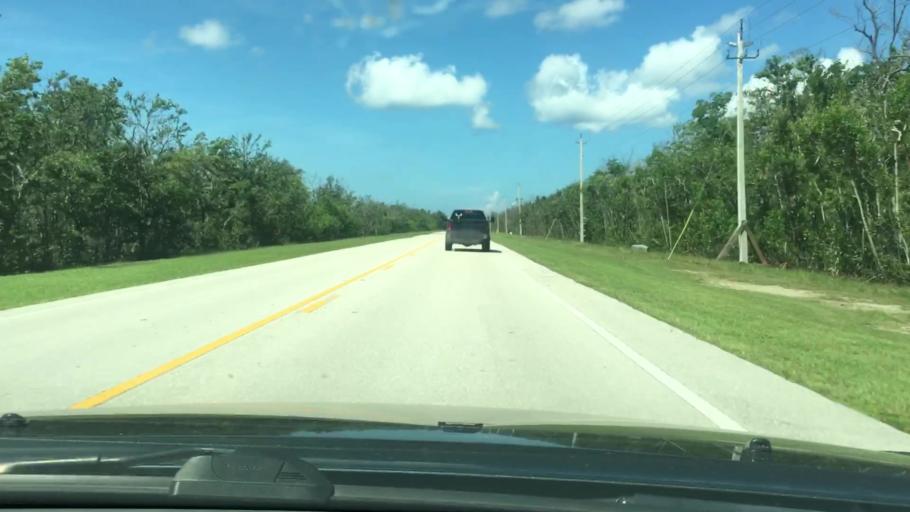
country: US
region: Florida
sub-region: Collier County
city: Marco
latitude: 25.9322
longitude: -81.6597
